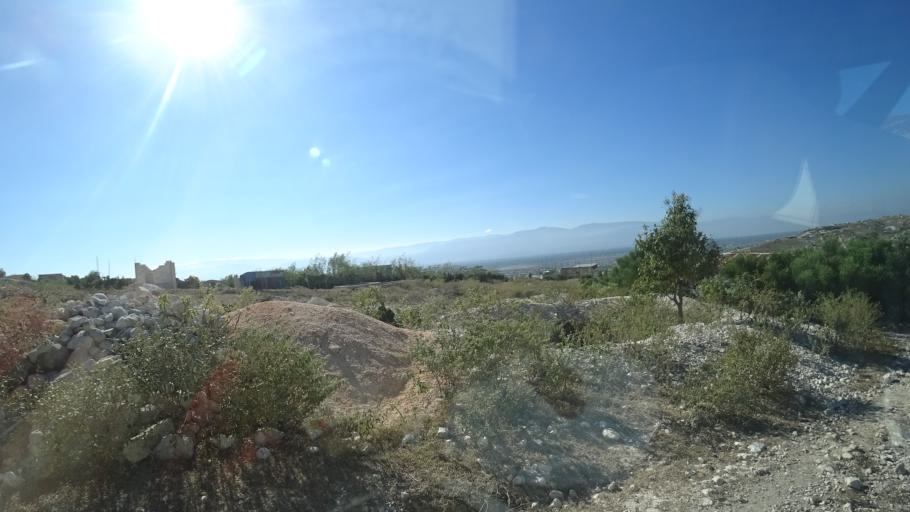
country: HT
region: Ouest
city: Croix des Bouquets
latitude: 18.6770
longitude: -72.2389
